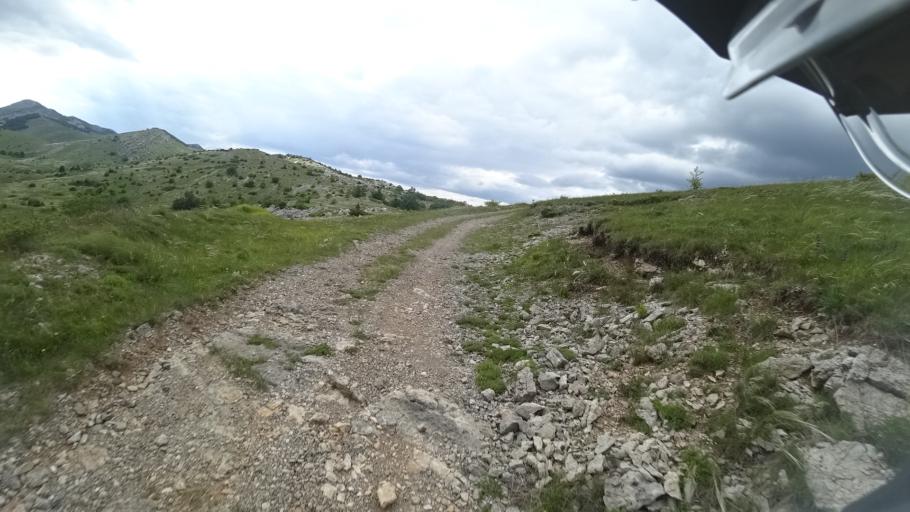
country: HR
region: Zadarska
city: Obrovac
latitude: 44.2671
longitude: 15.7293
